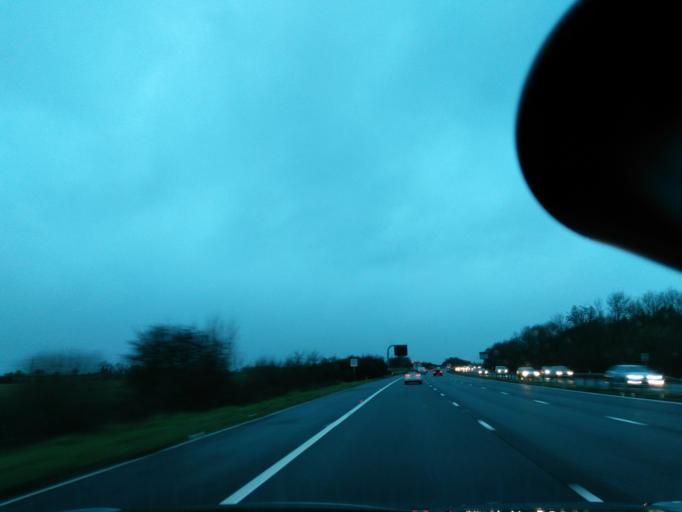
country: GB
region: England
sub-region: Wiltshire
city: Nettleton
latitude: 51.5126
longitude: -2.2883
